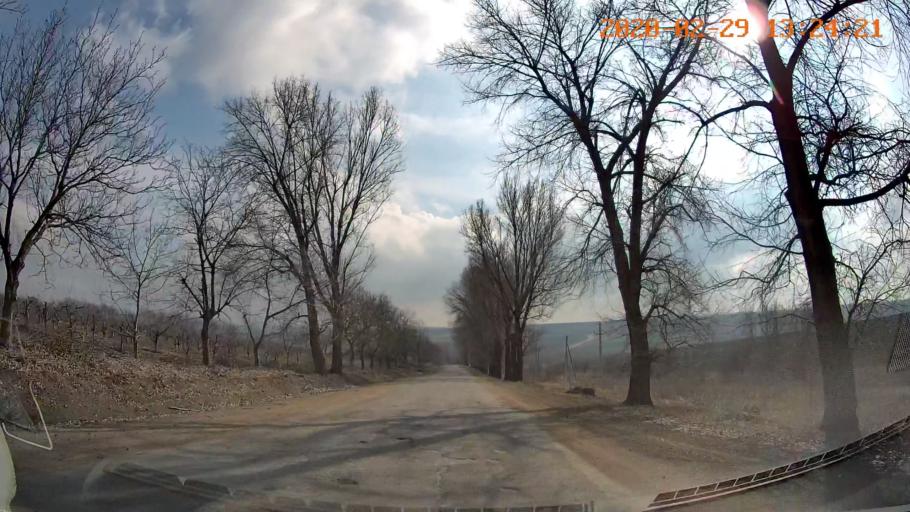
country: MD
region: Telenesti
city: Camenca
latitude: 47.9398
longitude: 28.6270
